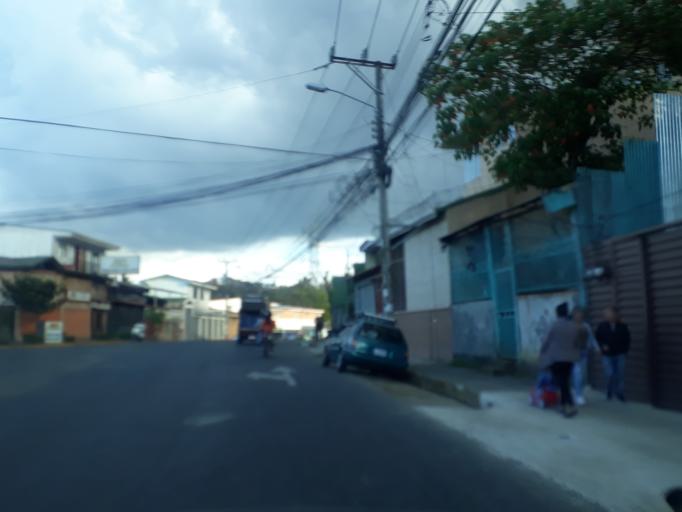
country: CR
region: San Jose
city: Purral
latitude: 9.9566
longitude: -84.0368
